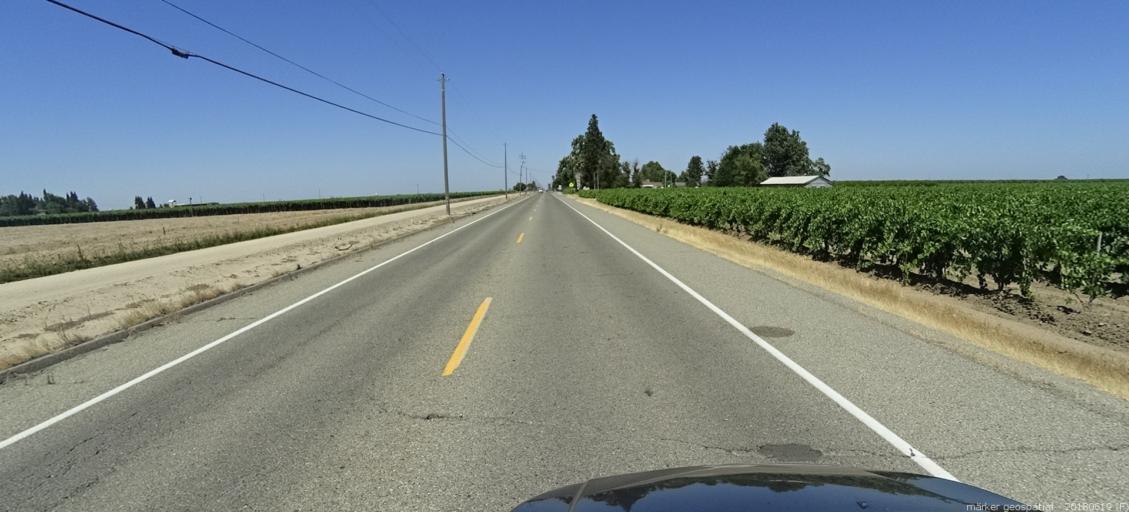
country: US
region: California
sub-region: Fresno County
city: Biola
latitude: 36.8513
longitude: -120.0683
